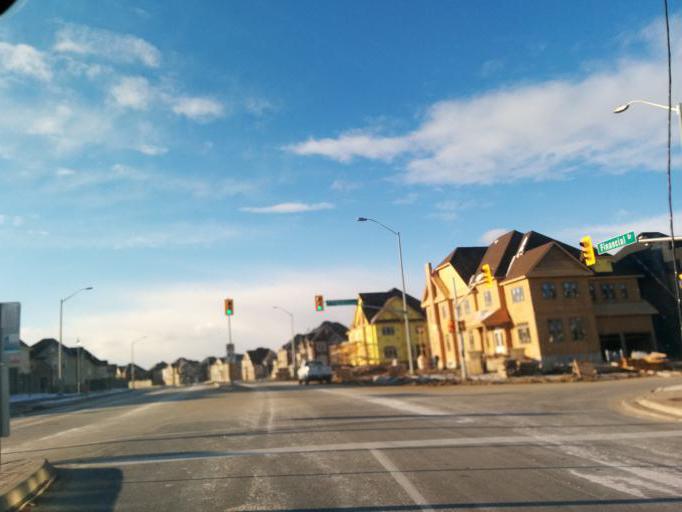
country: CA
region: Ontario
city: Brampton
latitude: 43.6358
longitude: -79.7793
